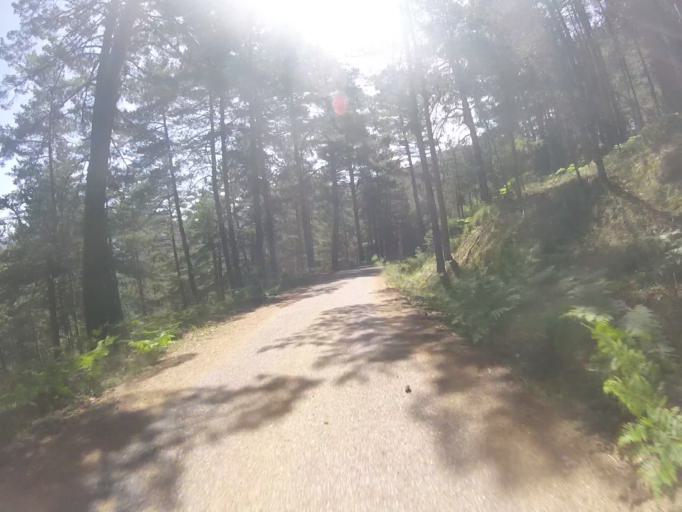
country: ES
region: Madrid
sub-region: Provincia de Madrid
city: Cercedilla
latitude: 40.8082
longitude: -4.0438
